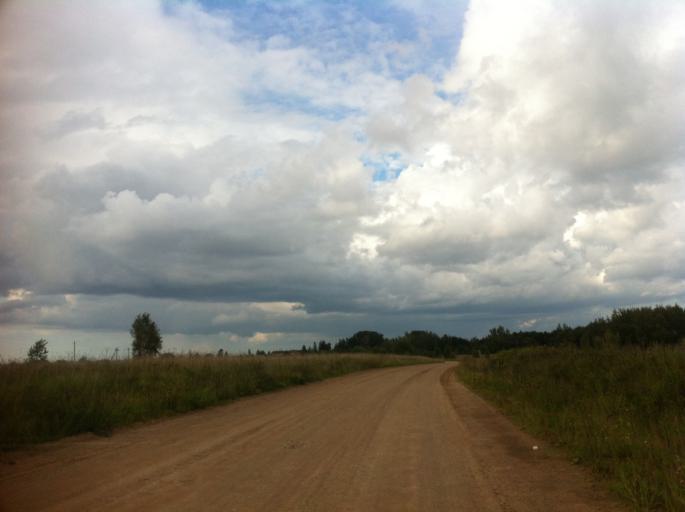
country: RU
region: Pskov
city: Izborsk
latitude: 57.8326
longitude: 27.9837
